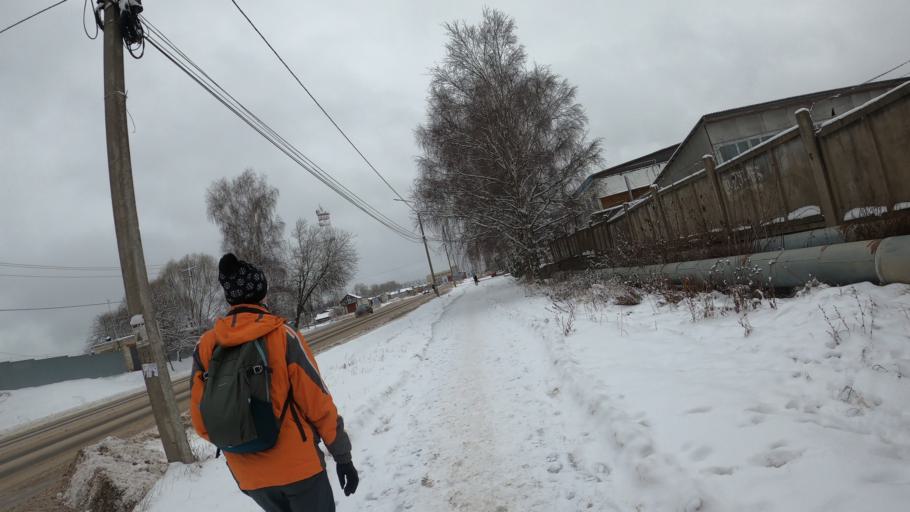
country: RU
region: Jaroslavl
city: Pereslavl'-Zalesskiy
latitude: 56.7421
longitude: 38.8915
